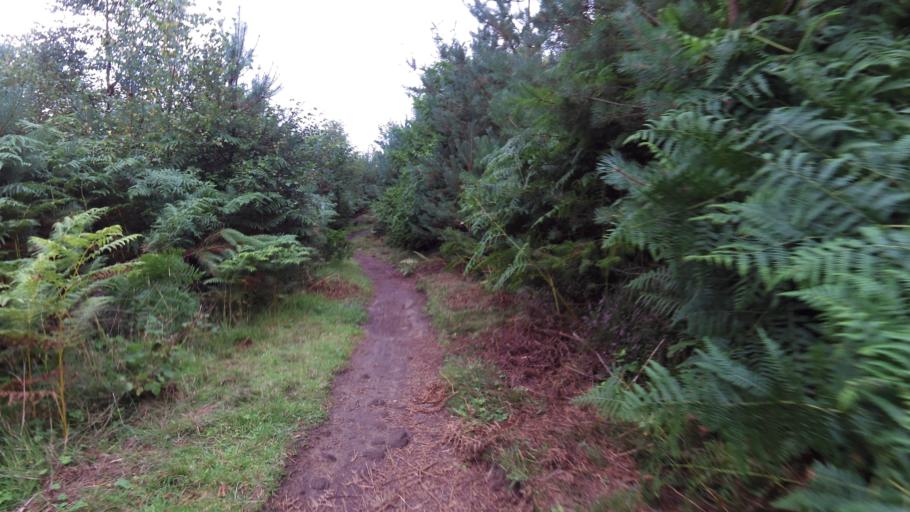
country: GB
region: England
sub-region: North Yorkshire
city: Thornton Dale
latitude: 54.2848
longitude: -0.6859
